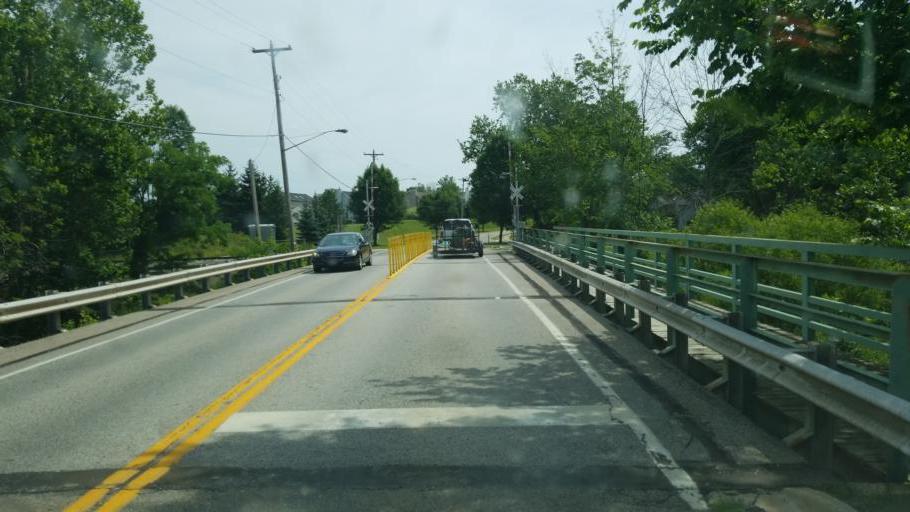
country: US
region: Ohio
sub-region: Summit County
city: Twinsburg
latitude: 41.3406
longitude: -81.4549
